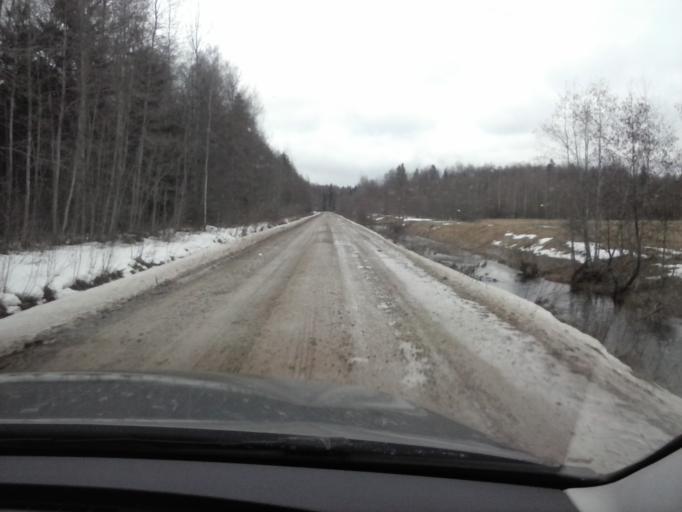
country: EE
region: Jogevamaa
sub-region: Mustvee linn
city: Mustvee
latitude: 59.0747
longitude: 26.8822
